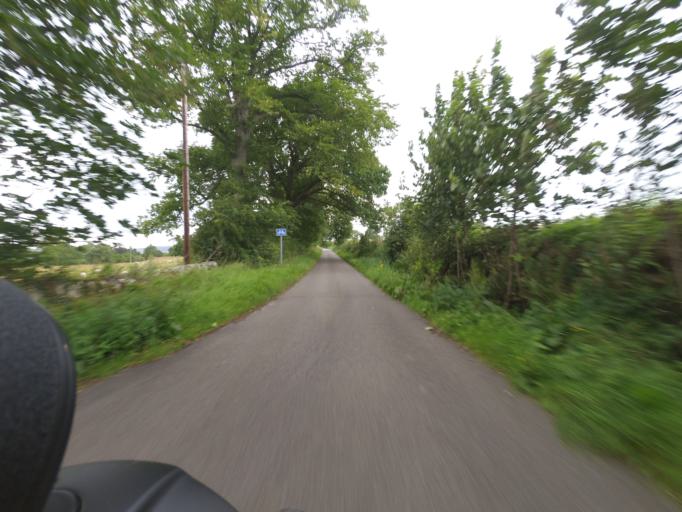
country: GB
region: Scotland
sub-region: Highland
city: Conon Bridge
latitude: 57.5137
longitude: -4.3686
